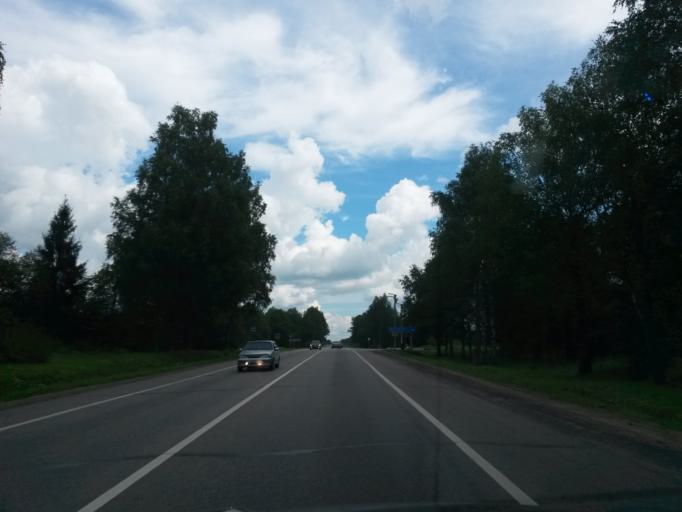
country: RU
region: Vladimir
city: Balakirevo
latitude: 56.6263
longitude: 38.6635
